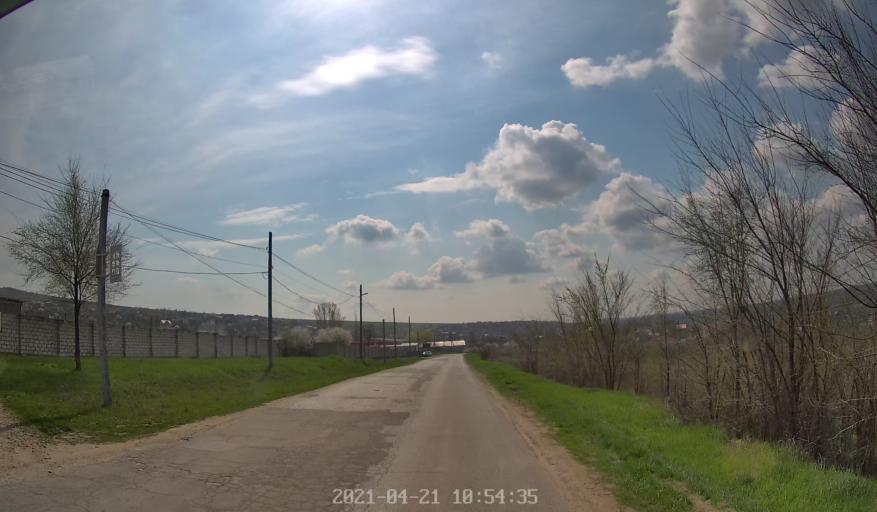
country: MD
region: Chisinau
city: Singera
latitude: 46.9720
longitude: 28.9378
